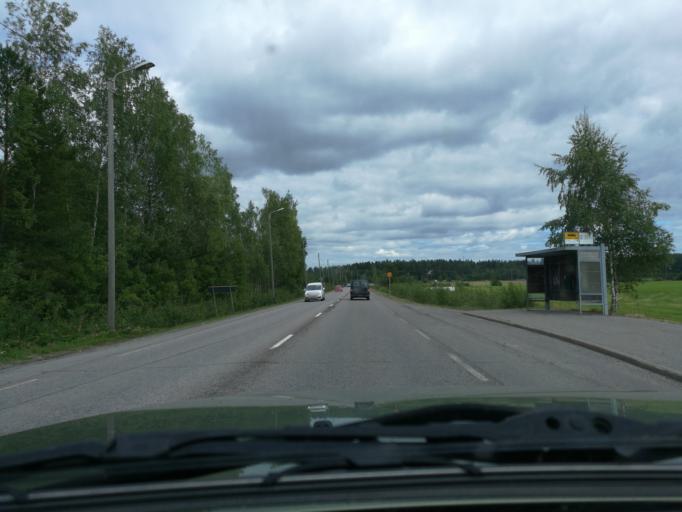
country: FI
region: Uusimaa
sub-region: Helsinki
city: Vantaa
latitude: 60.3144
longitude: 25.0785
